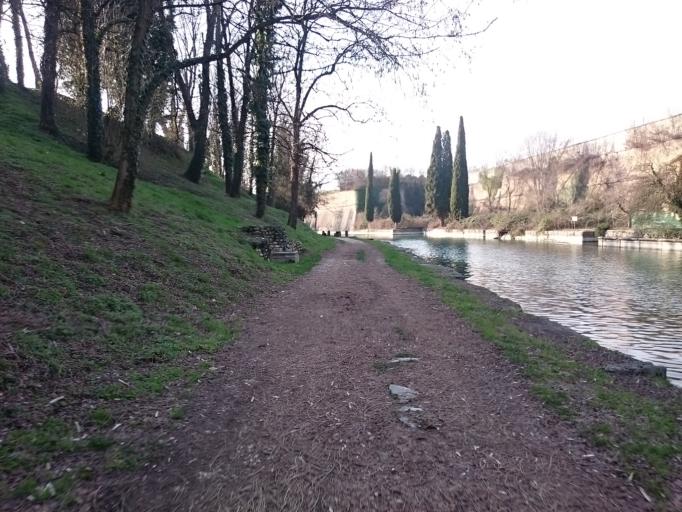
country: IT
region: Veneto
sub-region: Provincia di Verona
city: Peschiera del Garda
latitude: 45.4362
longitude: 10.6952
